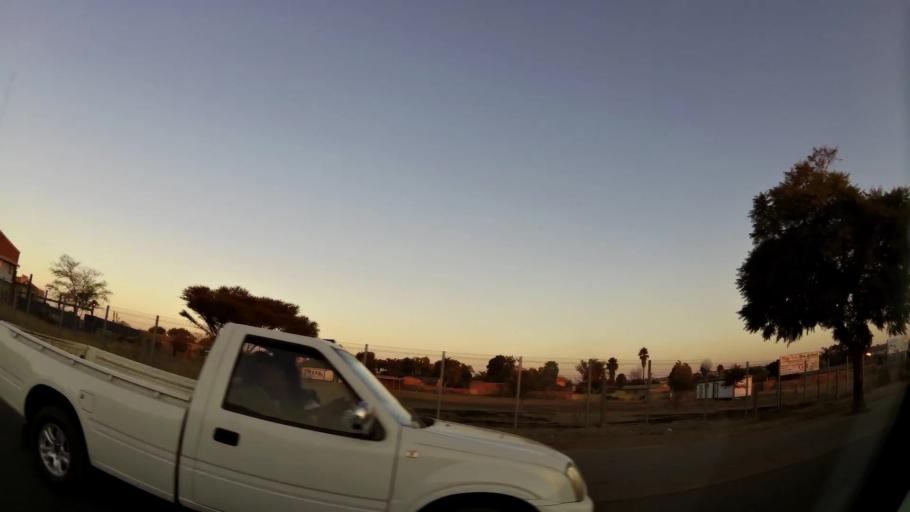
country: ZA
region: Gauteng
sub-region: City of Tshwane Metropolitan Municipality
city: Pretoria
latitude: -25.7293
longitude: 28.3201
